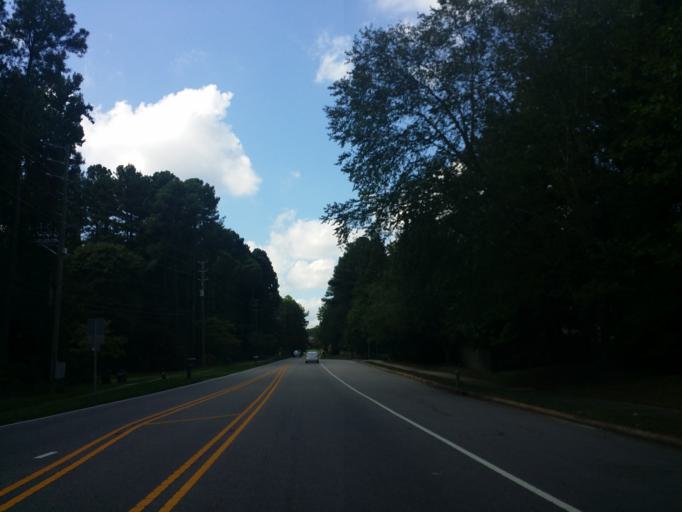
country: US
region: North Carolina
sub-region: Wake County
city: West Raleigh
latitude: 35.8859
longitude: -78.7106
